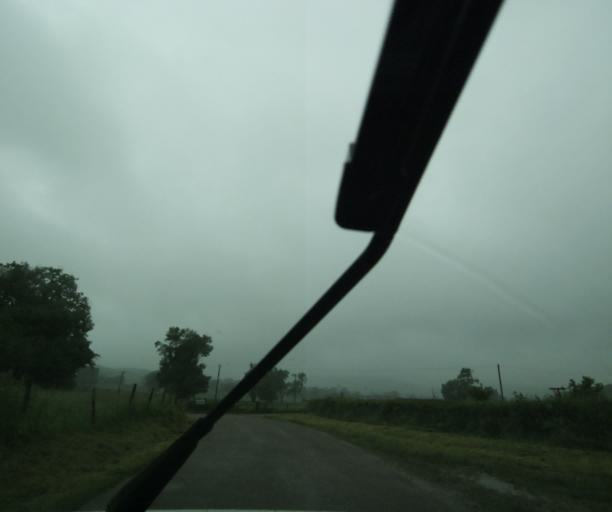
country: FR
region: Bourgogne
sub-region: Departement de Saone-et-Loire
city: Charolles
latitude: 46.3834
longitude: 4.2942
